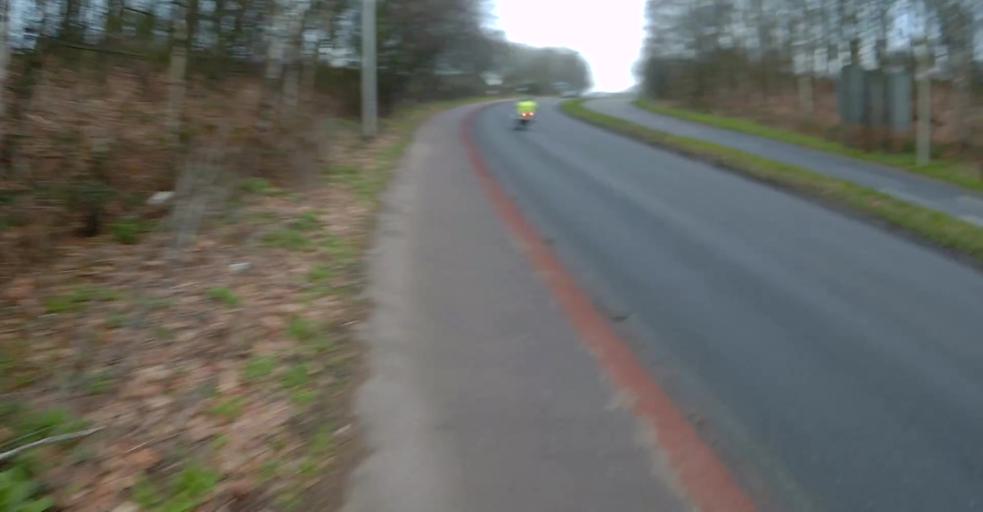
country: GB
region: England
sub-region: Bracknell Forest
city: Binfield
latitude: 51.4144
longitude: -0.7974
